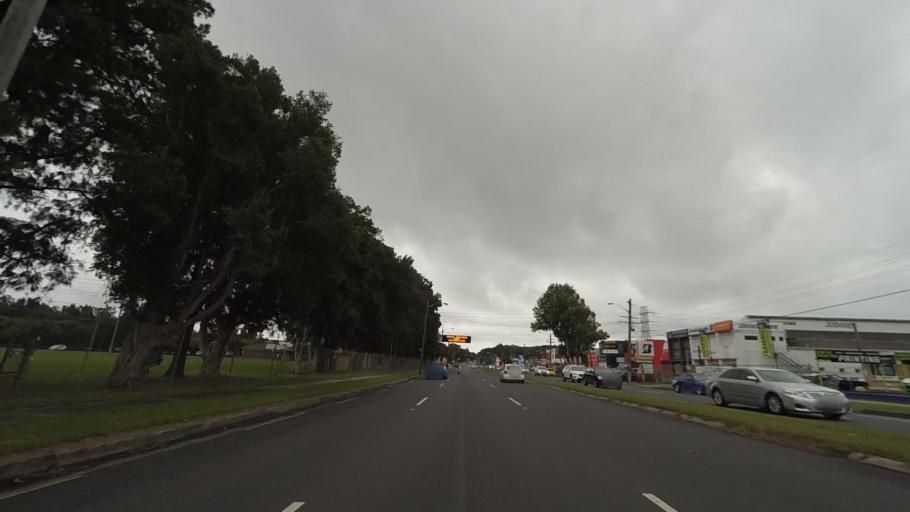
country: AU
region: New South Wales
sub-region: Sutherland Shire
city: Caringbah
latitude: -34.0228
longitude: 151.1211
